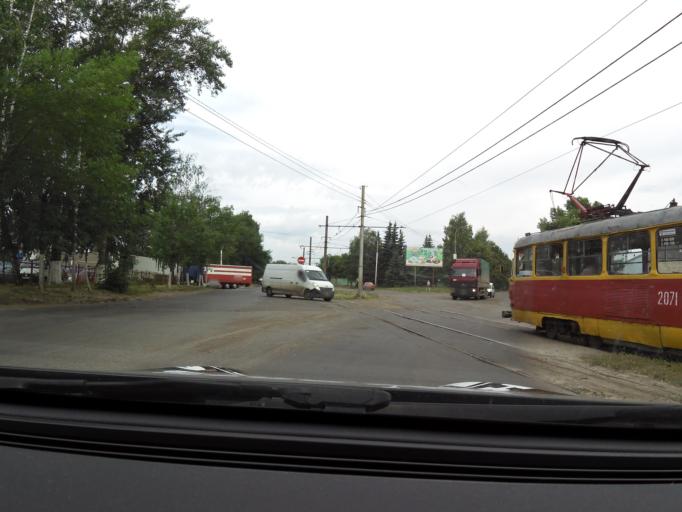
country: RU
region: Bashkortostan
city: Ufa
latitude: 54.7993
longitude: 56.1094
